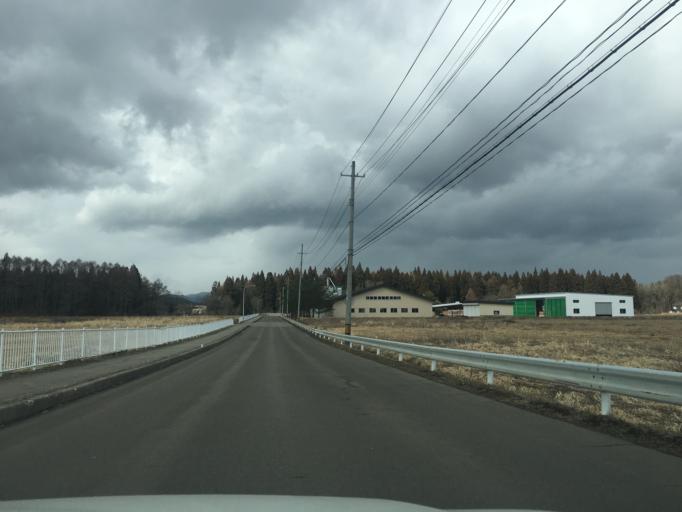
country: JP
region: Akita
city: Takanosu
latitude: 40.1838
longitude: 140.3415
